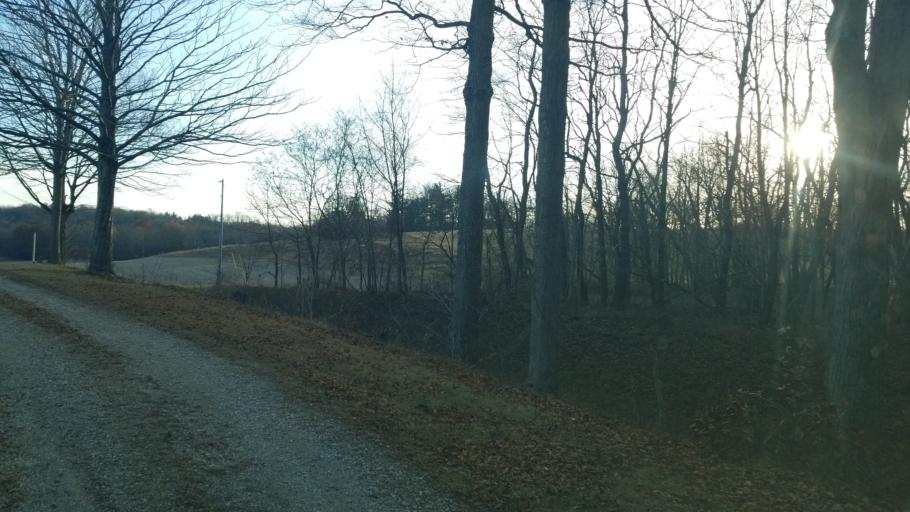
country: US
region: Ohio
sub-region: Licking County
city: Utica
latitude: 40.1896
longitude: -82.4428
